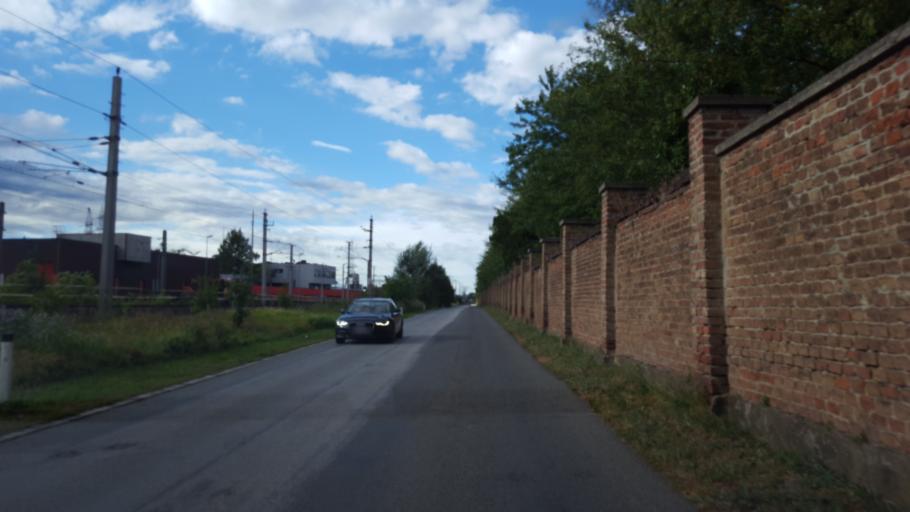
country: AT
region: Lower Austria
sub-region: Politischer Bezirk Wien-Umgebung
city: Schwechat
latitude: 48.1490
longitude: 16.4296
